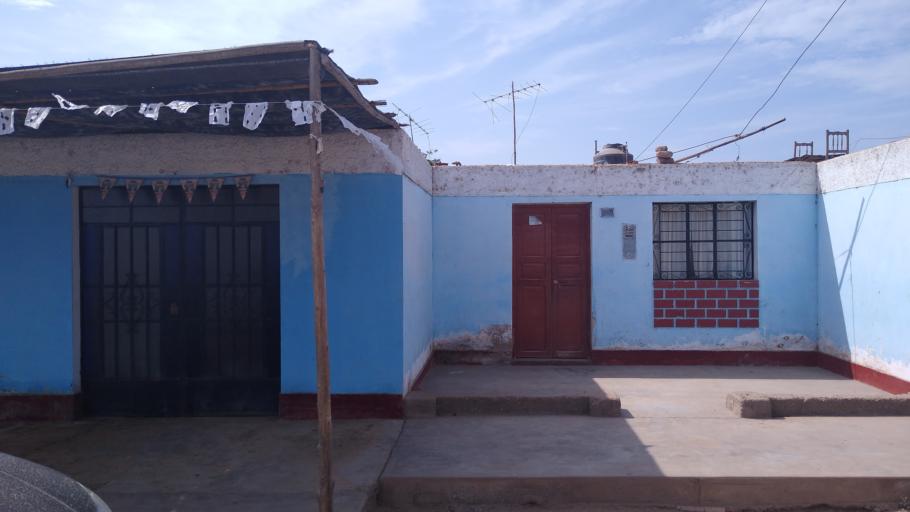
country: PE
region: Lima
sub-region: Provincia de Canete
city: Quilmana
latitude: -12.9461
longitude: -76.3849
